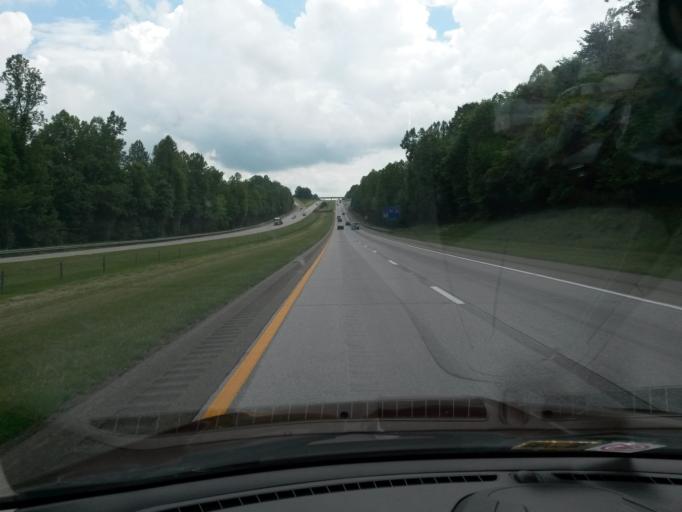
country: US
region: North Carolina
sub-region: Surry County
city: Elkin
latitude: 36.2900
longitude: -80.8163
